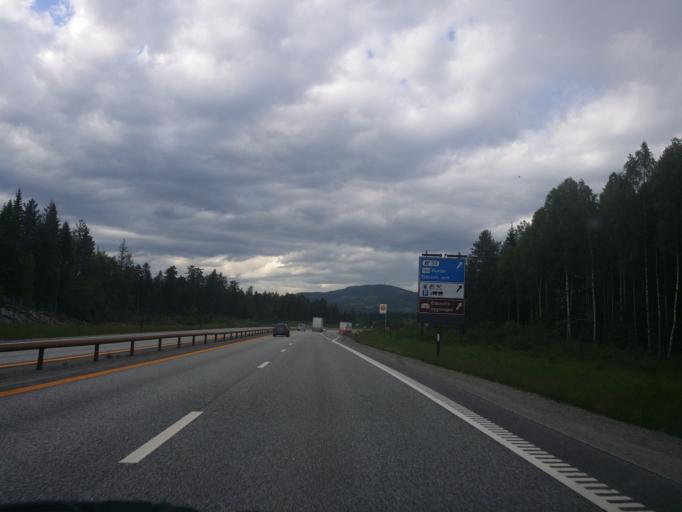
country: NO
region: Akershus
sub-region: Eidsvoll
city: Raholt
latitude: 60.3073
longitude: 11.1415
